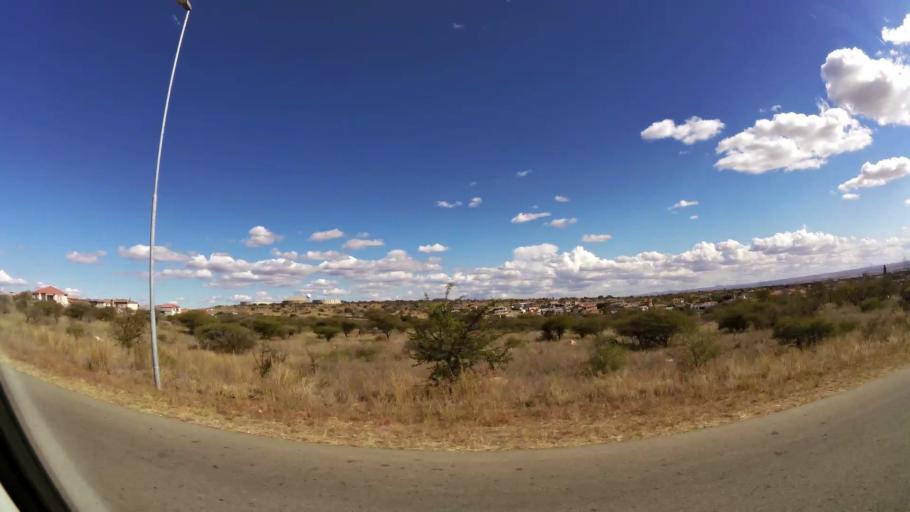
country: ZA
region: Limpopo
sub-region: Capricorn District Municipality
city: Polokwane
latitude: -23.8841
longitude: 29.5112
